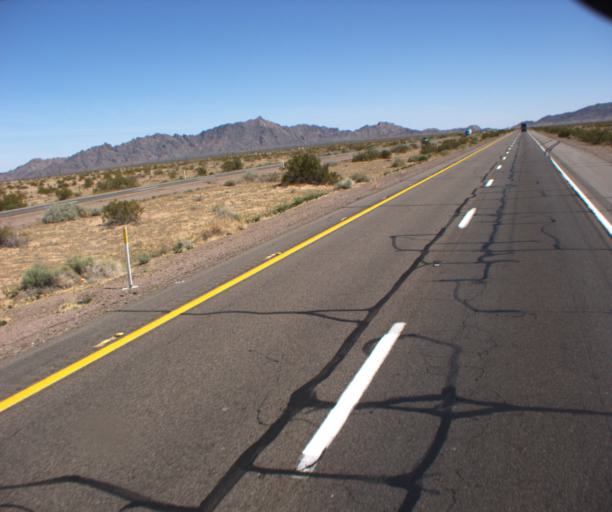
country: US
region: Arizona
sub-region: Yuma County
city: Wellton
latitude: 32.7119
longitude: -113.8315
